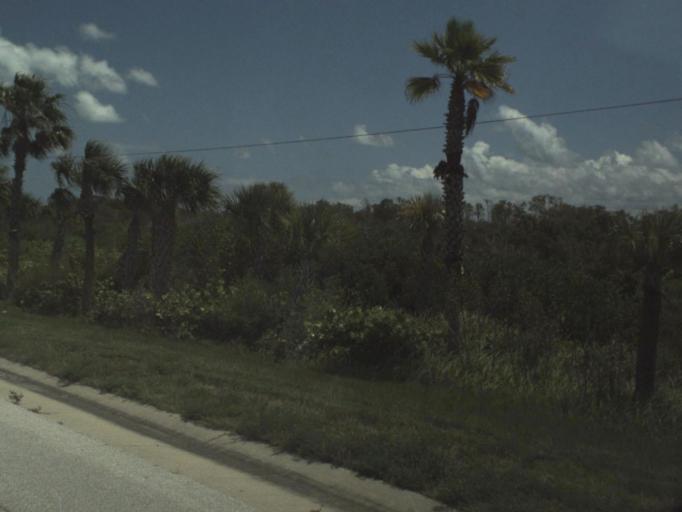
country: US
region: Florida
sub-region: Brevard County
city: Cape Canaveral
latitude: 28.4056
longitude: -80.6285
